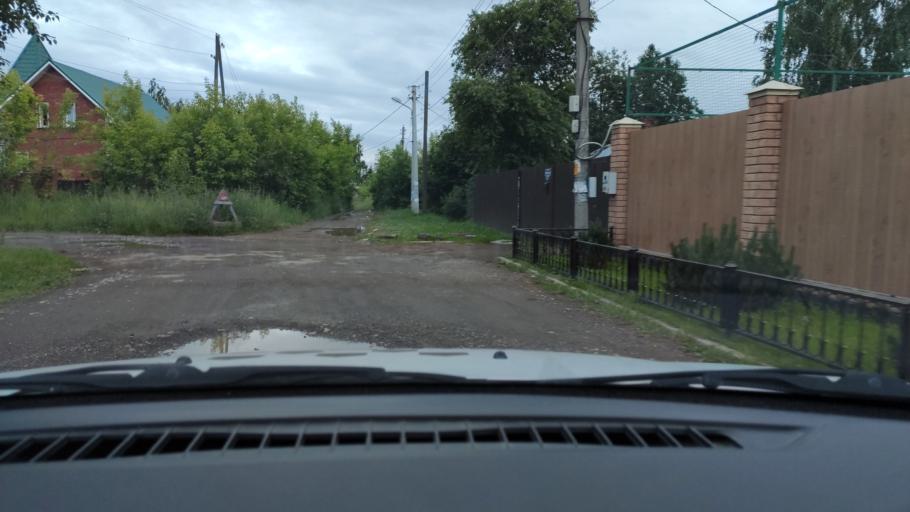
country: RU
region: Perm
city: Perm
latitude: 58.0183
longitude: 56.3104
